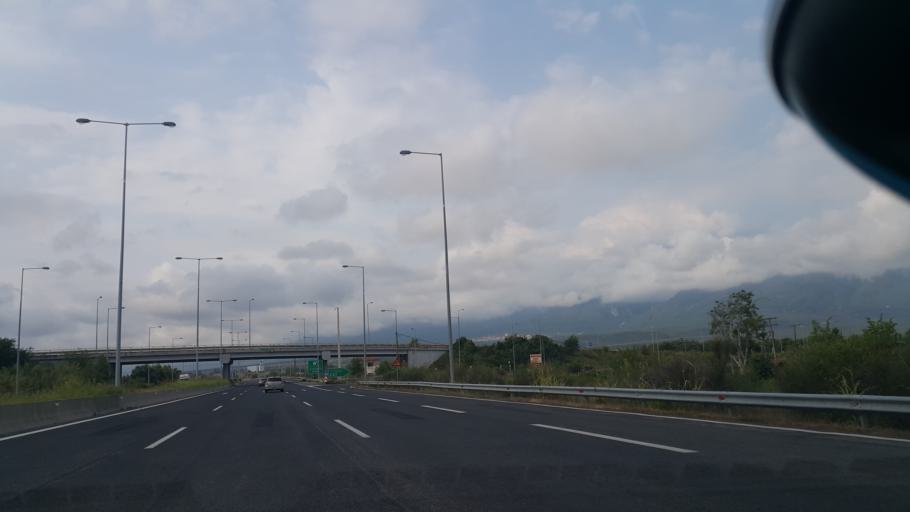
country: GR
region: Central Macedonia
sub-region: Nomos Pierias
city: Dion
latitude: 40.1527
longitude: 22.5419
